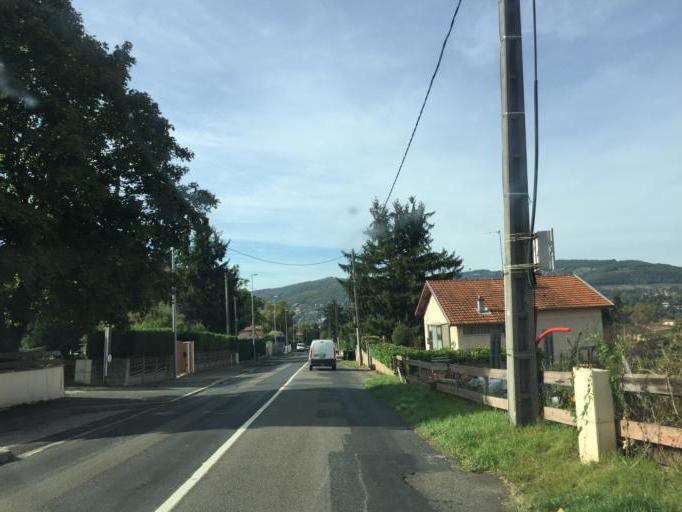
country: FR
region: Rhone-Alpes
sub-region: Departement du Rhone
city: Neuville-sur-Saone
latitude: 45.8790
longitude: 4.8524
